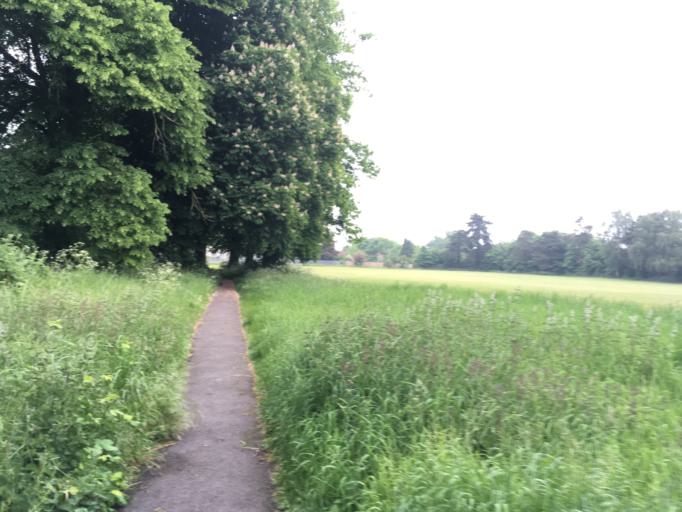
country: GB
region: England
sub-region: South Gloucestershire
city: Thornbury
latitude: 51.6098
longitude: -2.5215
